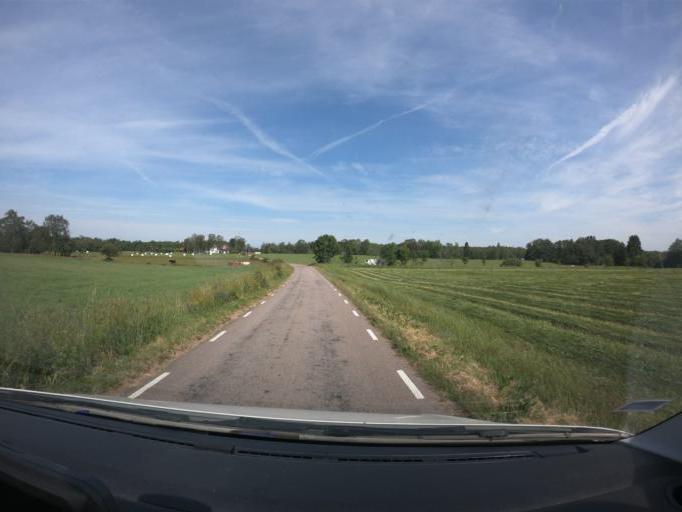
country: SE
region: Skane
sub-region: Bastads Kommun
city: Bastad
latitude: 56.3883
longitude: 12.9580
